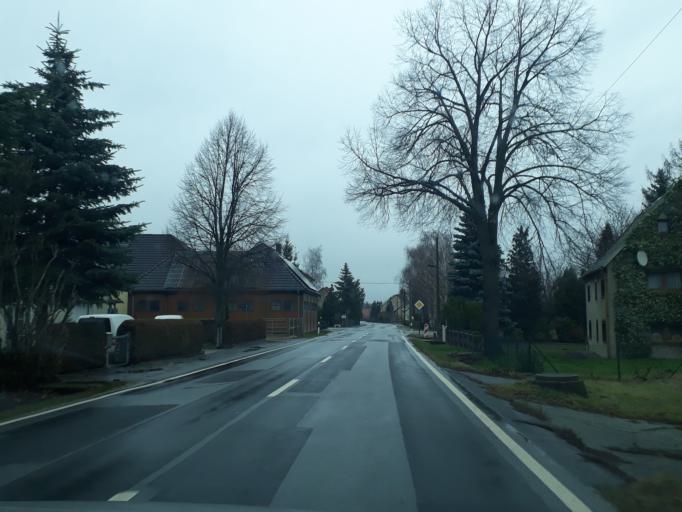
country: DE
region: Saxony
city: Malschwitz
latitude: 51.2254
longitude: 14.5049
